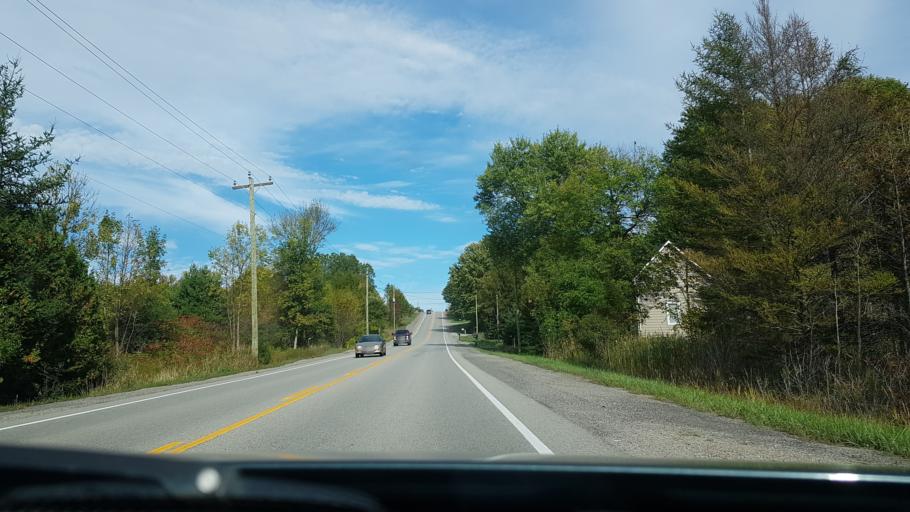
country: CA
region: Ontario
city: Angus
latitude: 44.4816
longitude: -79.8312
